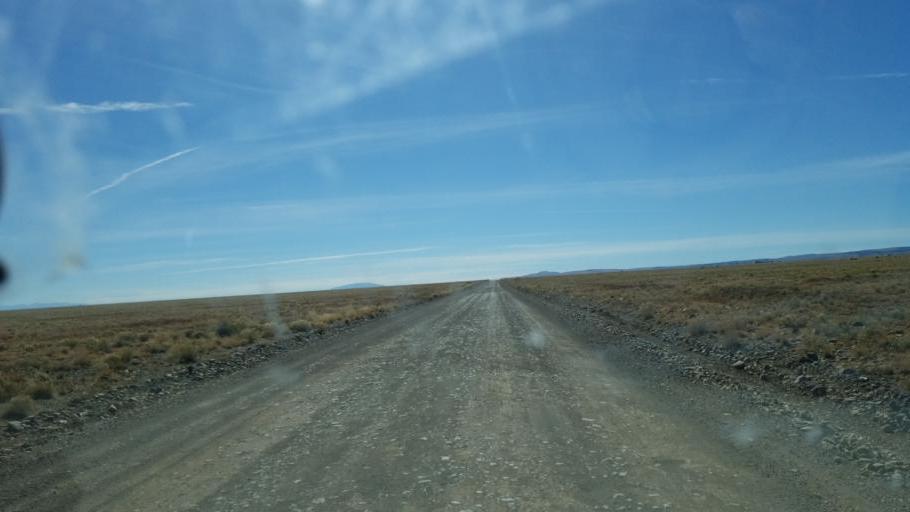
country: US
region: Colorado
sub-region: Rio Grande County
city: Monte Vista
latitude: 37.3683
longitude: -106.1493
